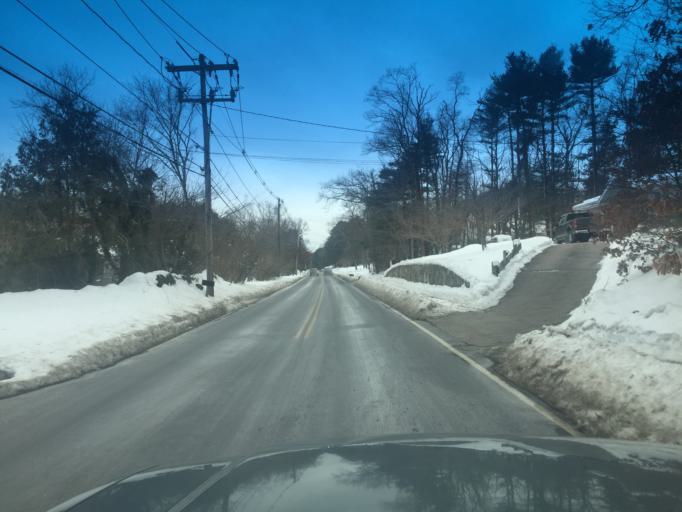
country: US
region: Massachusetts
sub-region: Norfolk County
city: Norfolk
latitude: 42.1079
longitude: -71.2835
